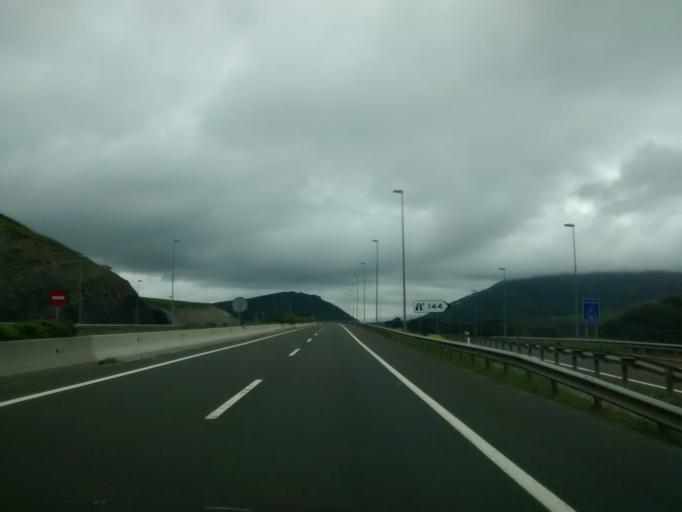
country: ES
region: Cantabria
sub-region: Provincia de Cantabria
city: Santiurde de Reinosa
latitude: 43.0648
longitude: -4.0890
